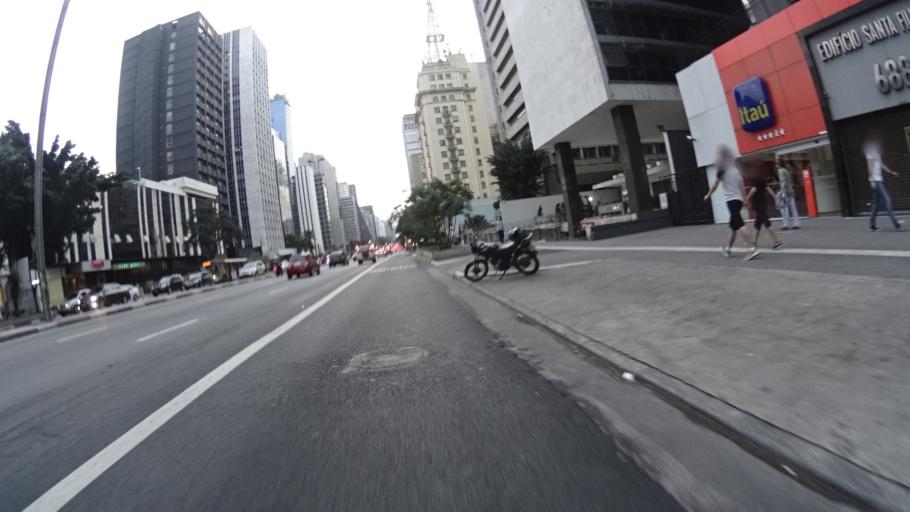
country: BR
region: Sao Paulo
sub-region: Sao Paulo
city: Sao Paulo
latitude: -23.5671
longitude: -46.6496
